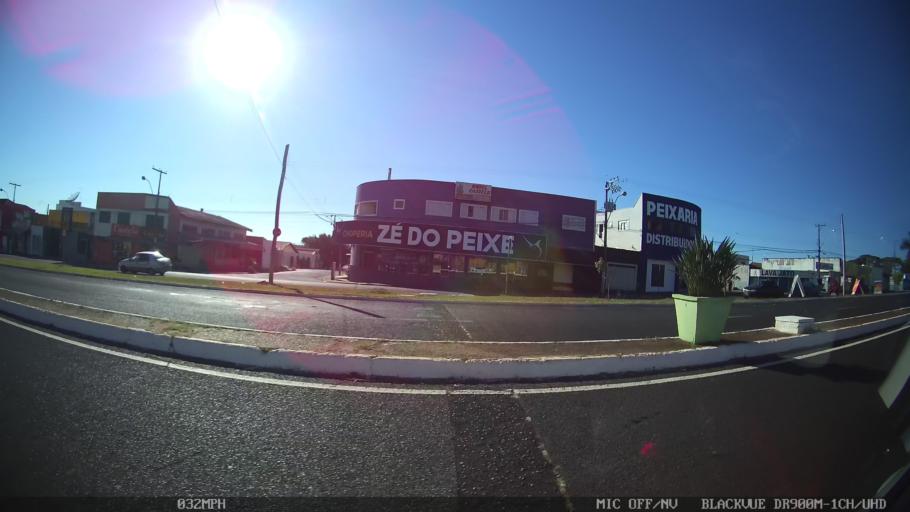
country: BR
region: Sao Paulo
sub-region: Franca
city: Franca
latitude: -20.5595
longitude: -47.3956
